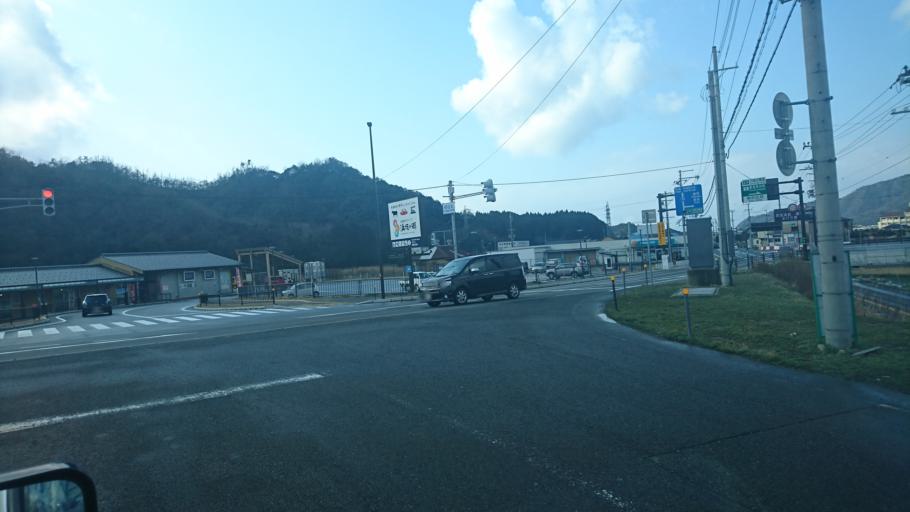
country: JP
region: Tottori
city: Tottori
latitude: 35.6102
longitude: 134.4705
